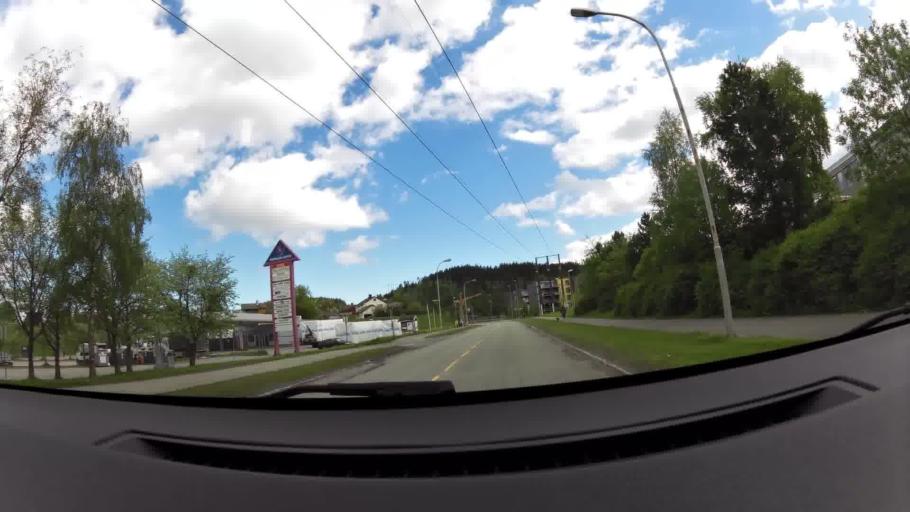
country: NO
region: Sor-Trondelag
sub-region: Trondheim
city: Trondheim
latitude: 63.3907
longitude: 10.4309
